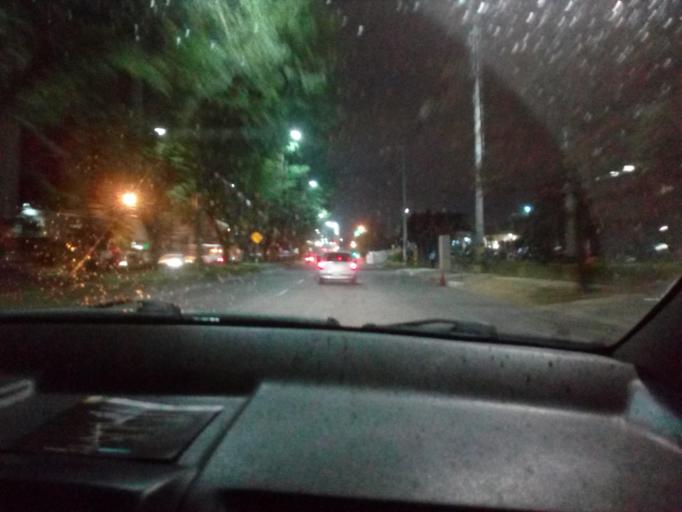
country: CO
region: Antioquia
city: Envigado
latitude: 6.1766
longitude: -75.5904
